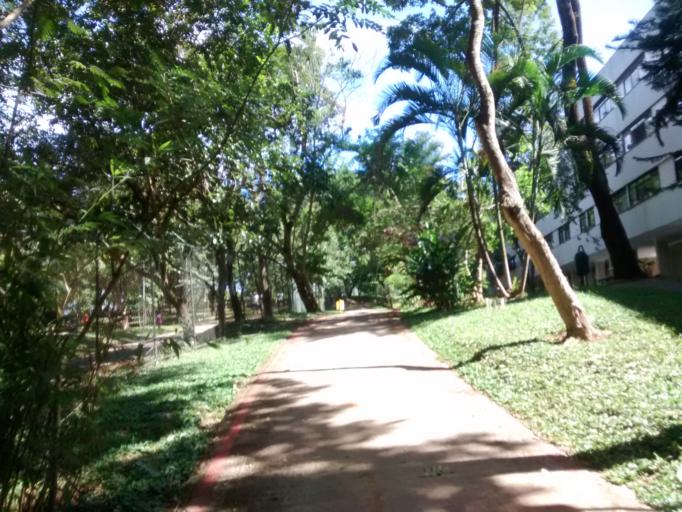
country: BR
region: Federal District
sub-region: Brasilia
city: Brasilia
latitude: -15.7409
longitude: -47.8860
